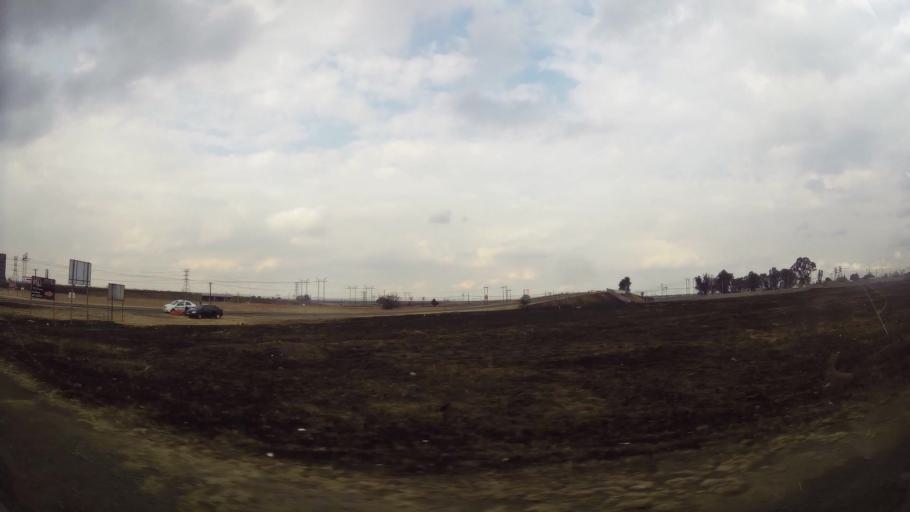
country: ZA
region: Orange Free State
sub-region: Fezile Dabi District Municipality
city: Sasolburg
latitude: -26.8408
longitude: 27.8717
